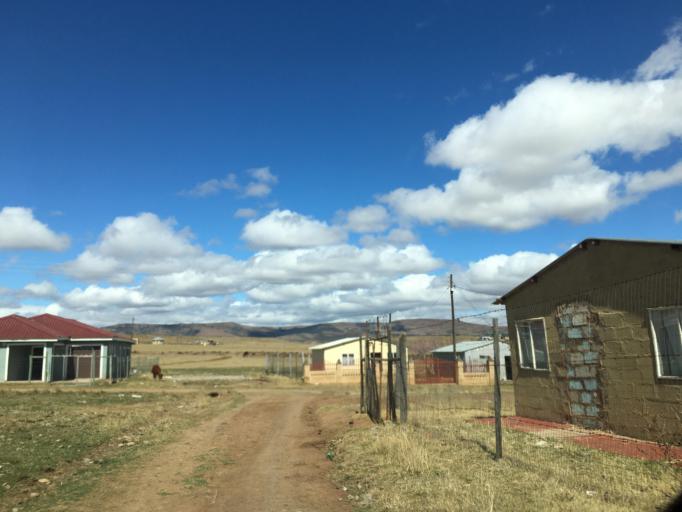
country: ZA
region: Eastern Cape
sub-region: Chris Hani District Municipality
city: Cala
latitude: -31.5415
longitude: 27.6779
